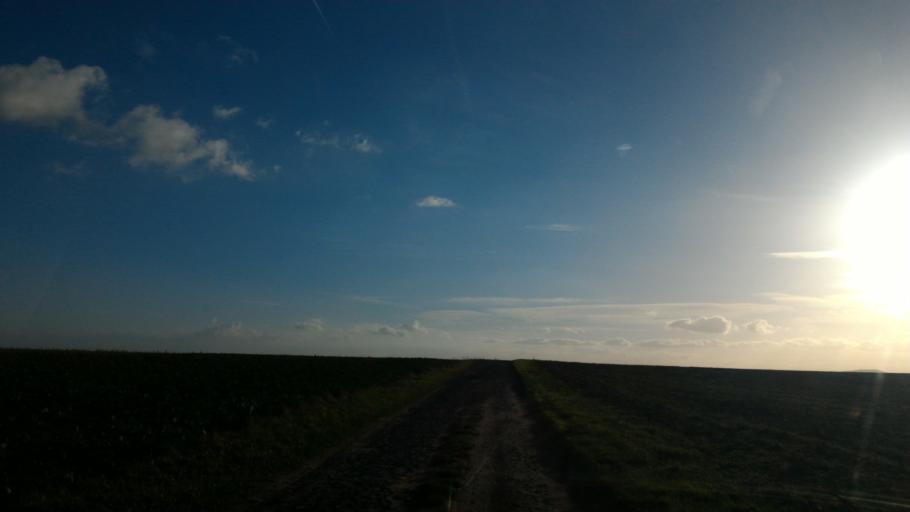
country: CZ
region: Central Bohemia
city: Bela pod Bezdezem
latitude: 50.5328
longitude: 14.7468
